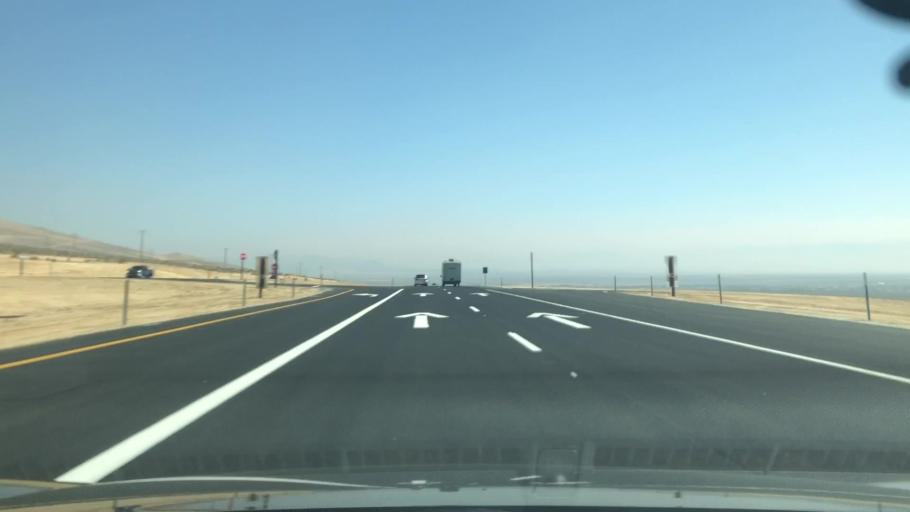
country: US
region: California
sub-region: Kern County
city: Inyokern
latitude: 35.6473
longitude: -117.8796
